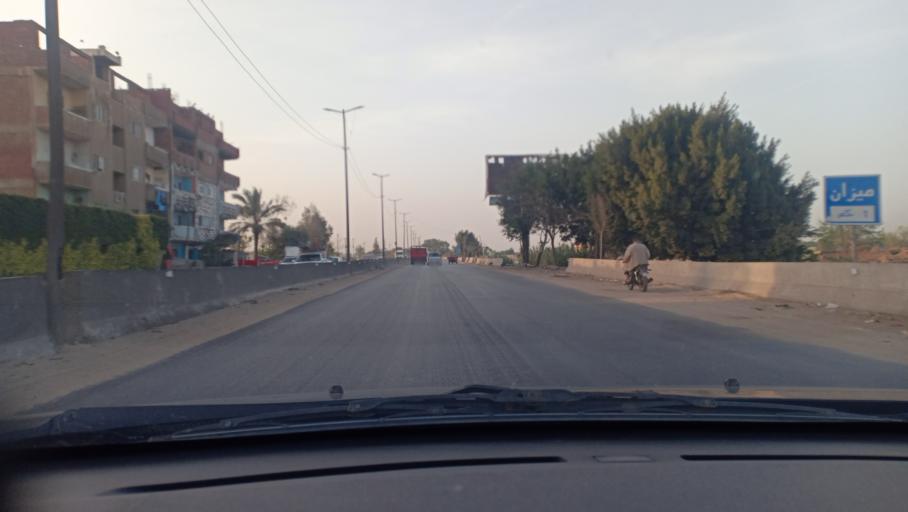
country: EG
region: Muhafazat al Minufiyah
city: Quwaysina
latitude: 30.5792
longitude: 31.2735
